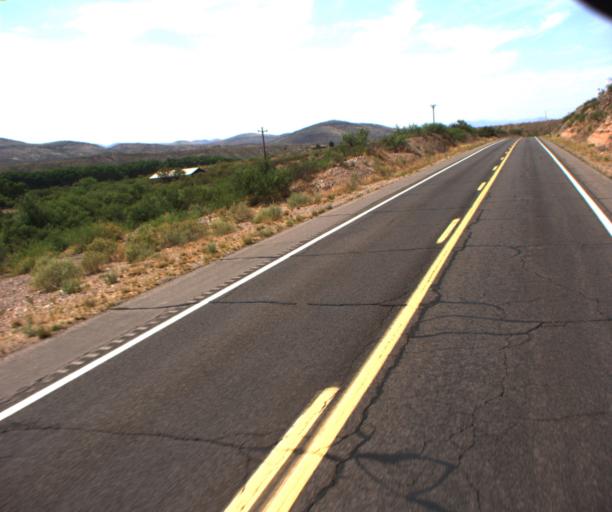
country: US
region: Arizona
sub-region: Greenlee County
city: Clifton
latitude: 32.8383
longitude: -109.1798
